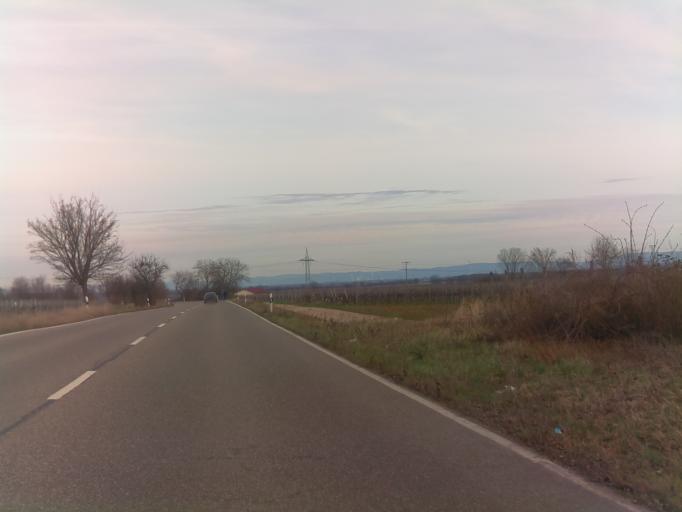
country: DE
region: Rheinland-Pfalz
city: Ruppertsberg
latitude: 49.3720
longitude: 8.1790
